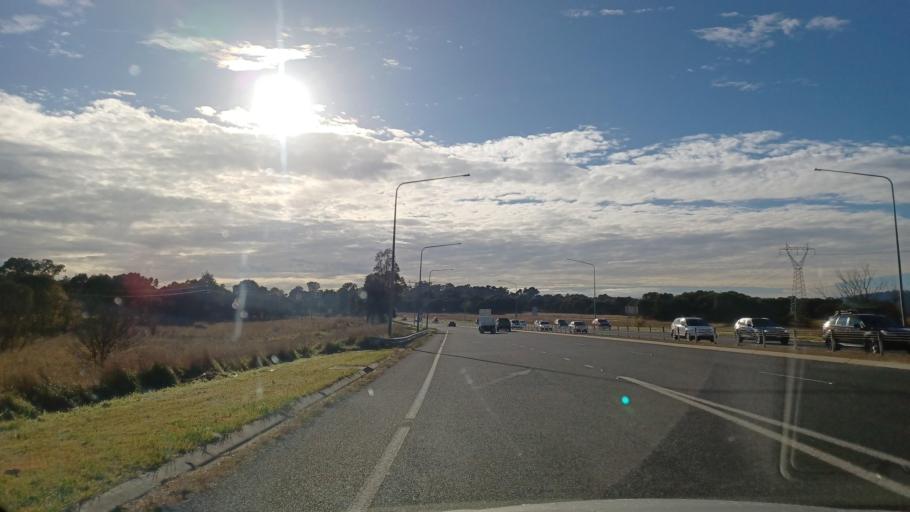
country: AU
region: Australian Capital Territory
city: Kaleen
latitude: -35.2242
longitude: 149.1254
